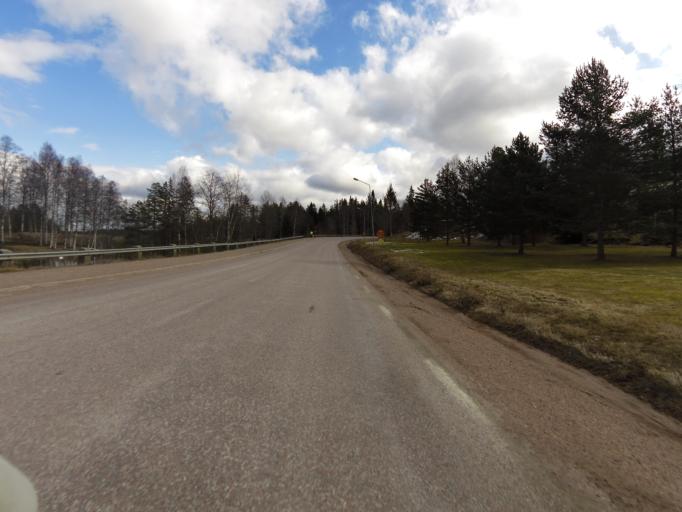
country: SE
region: Dalarna
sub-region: Avesta Kommun
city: Avesta
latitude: 60.3163
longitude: 16.2034
